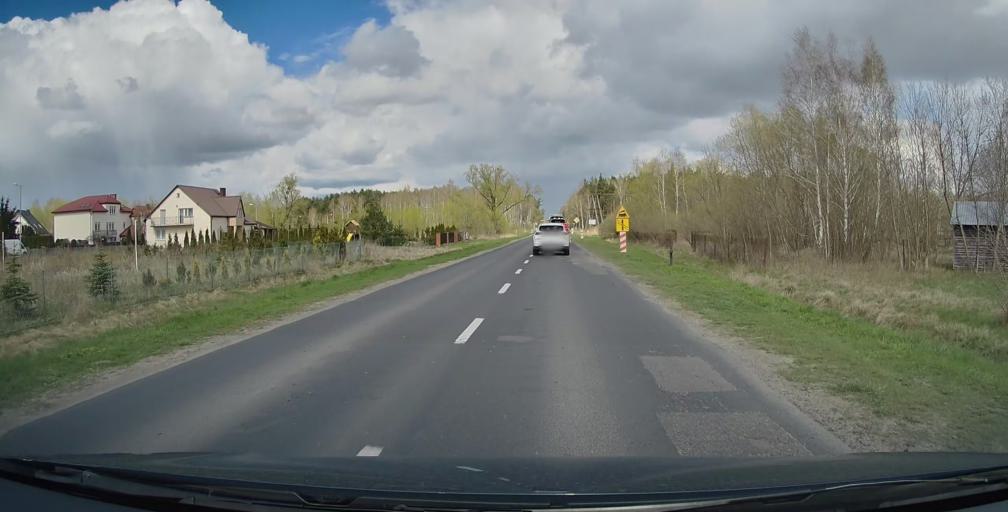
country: PL
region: Masovian Voivodeship
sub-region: Ostroleka
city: Ostroleka
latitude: 53.0549
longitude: 21.5866
